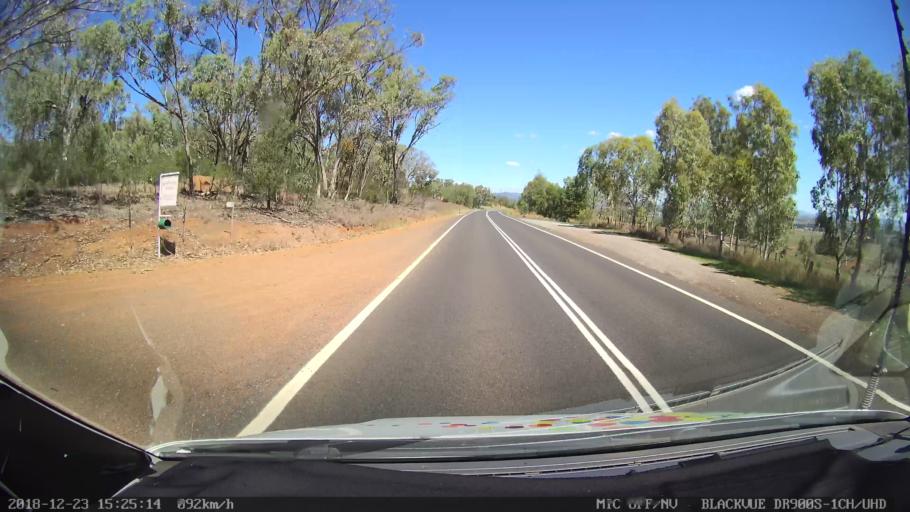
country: AU
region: New South Wales
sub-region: Tamworth Municipality
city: Manilla
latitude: -30.9015
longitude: 150.8288
